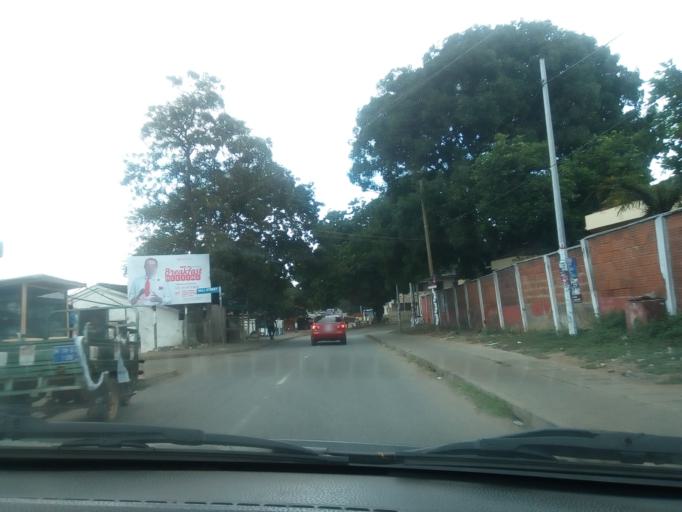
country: GH
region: Greater Accra
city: Accra
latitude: 5.5607
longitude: -0.2095
